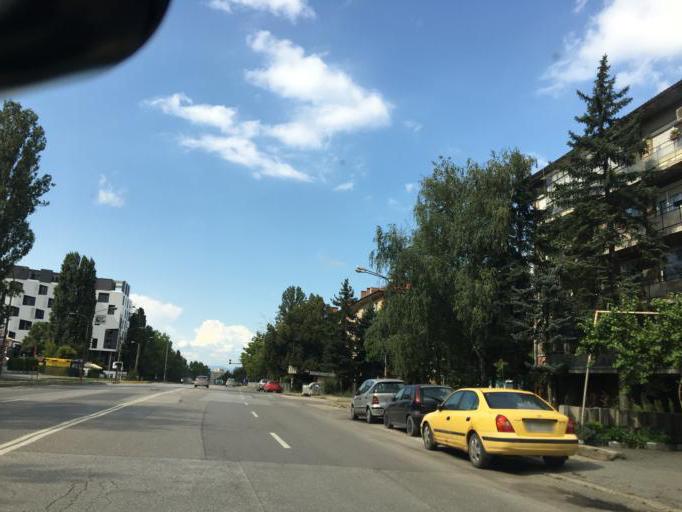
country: BG
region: Sofia-Capital
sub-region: Stolichna Obshtina
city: Sofia
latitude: 42.6558
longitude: 23.3592
